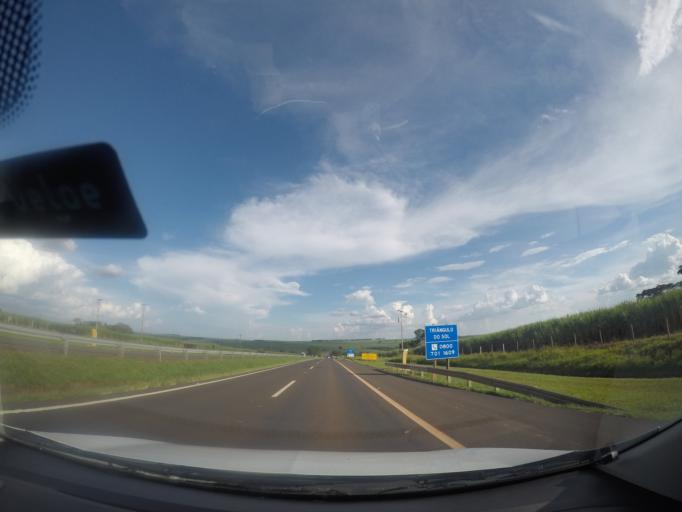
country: BR
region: Sao Paulo
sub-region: Jaboticabal
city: Jaboticabal
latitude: -21.3020
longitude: -48.3277
